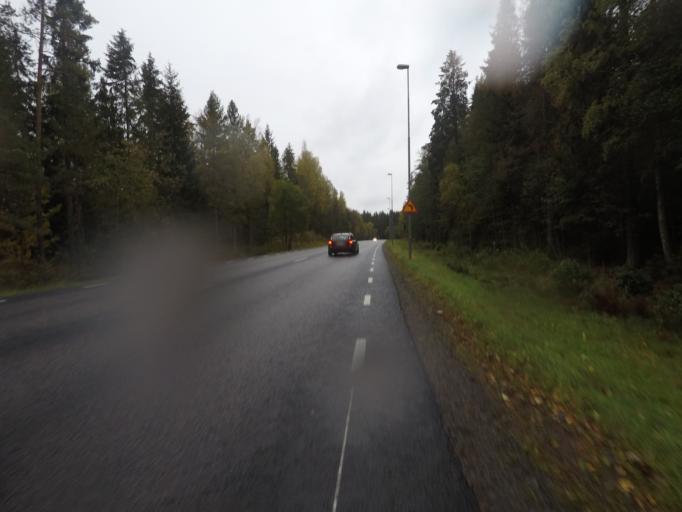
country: SE
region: OErebro
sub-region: Karlskoga Kommun
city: Karlskoga
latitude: 59.3090
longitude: 14.4679
